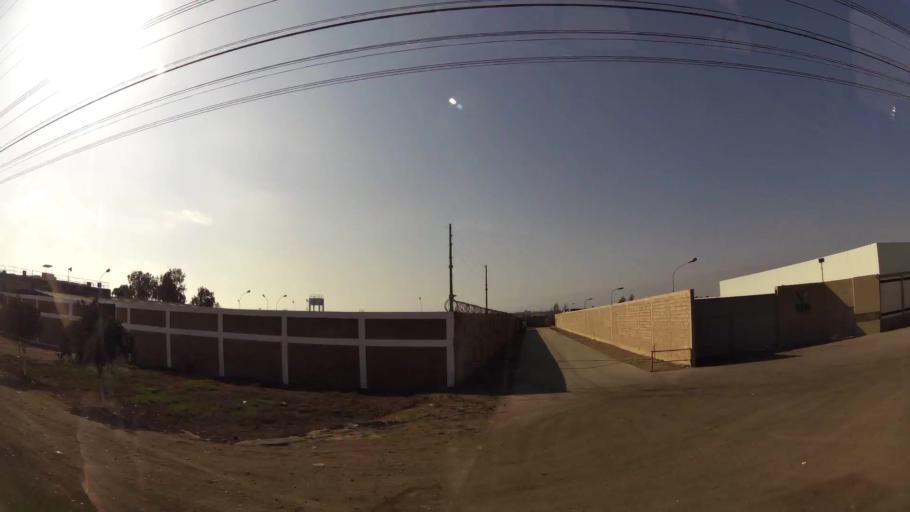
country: PE
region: Ica
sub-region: Provincia de Chincha
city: Chincha Baja
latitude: -13.4508
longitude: -76.1400
